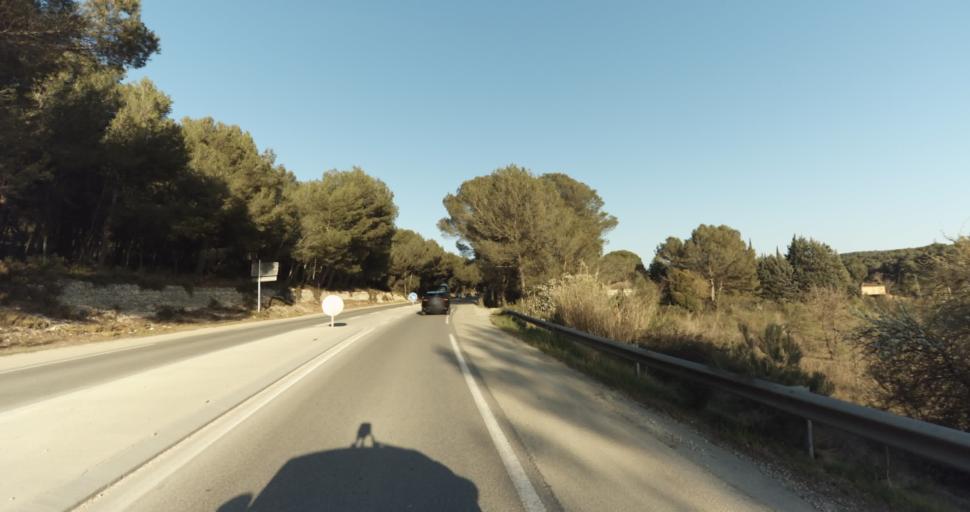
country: FR
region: Provence-Alpes-Cote d'Azur
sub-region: Departement des Bouches-du-Rhone
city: Ventabren
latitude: 43.5491
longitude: 5.3019
